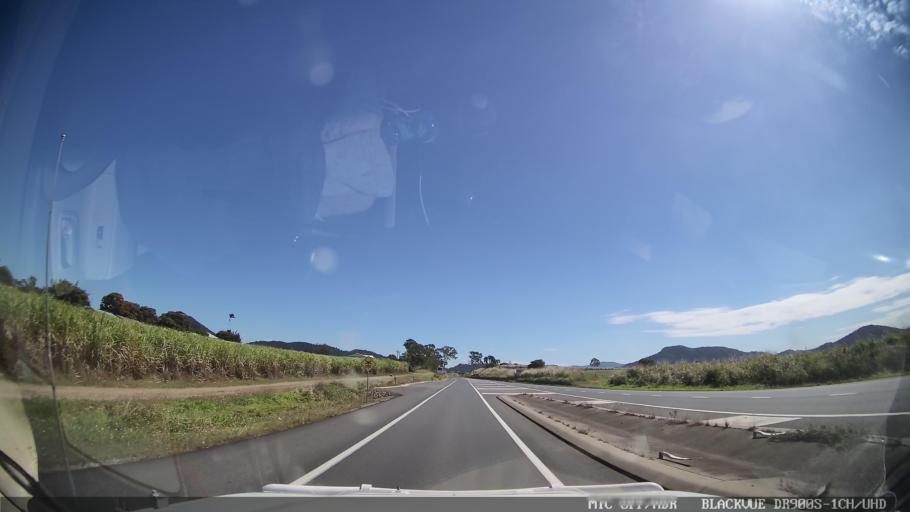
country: AU
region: Queensland
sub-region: Mackay
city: Walkerston
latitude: -21.0911
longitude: 149.0550
